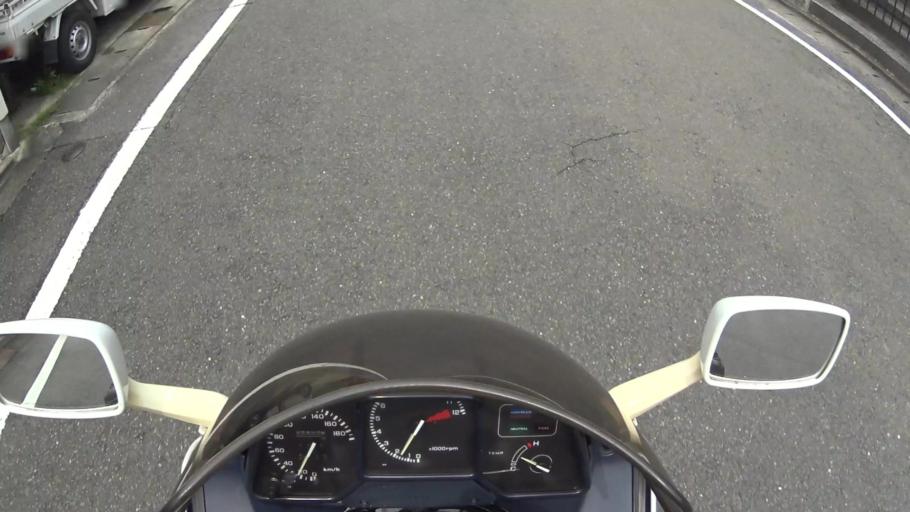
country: JP
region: Kyoto
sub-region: Kyoto-shi
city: Kamigyo-ku
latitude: 35.0441
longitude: 135.7938
